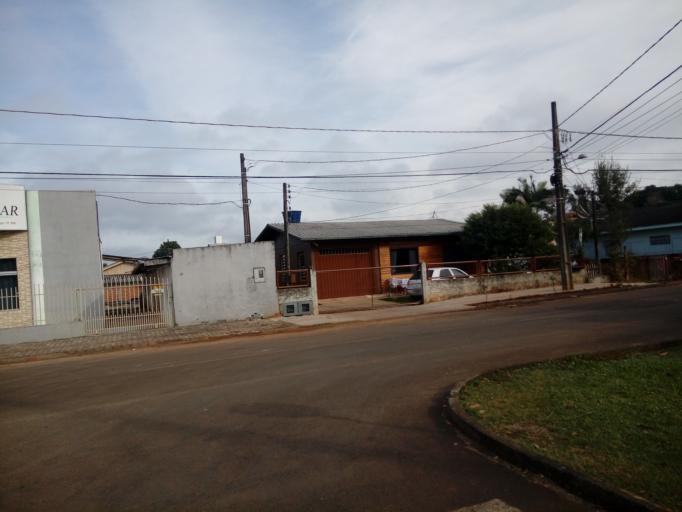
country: BR
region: Santa Catarina
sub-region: Chapeco
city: Chapeco
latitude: -27.1090
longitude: -52.6290
